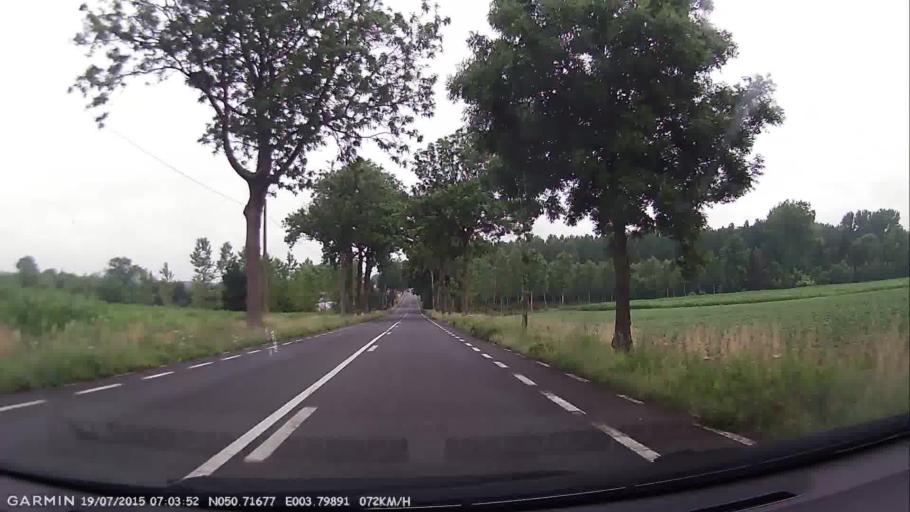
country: BE
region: Wallonia
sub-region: Province du Hainaut
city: Lessines
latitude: 50.7168
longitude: 3.7986
